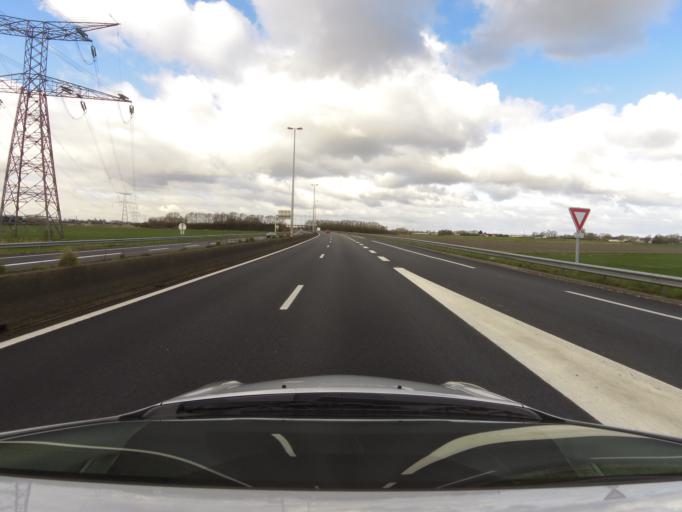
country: FR
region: Nord-Pas-de-Calais
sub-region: Departement du Pas-de-Calais
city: Saint-Folquin
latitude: 50.9517
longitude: 2.1231
